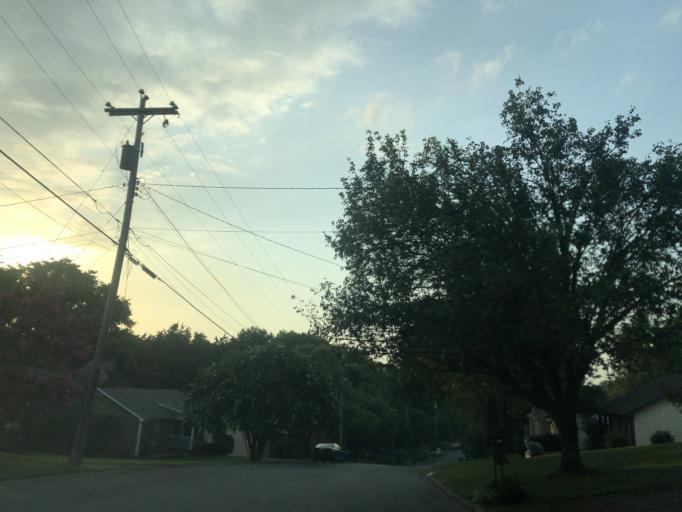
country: US
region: Tennessee
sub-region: Davidson County
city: Lakewood
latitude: 36.1368
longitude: -86.6311
